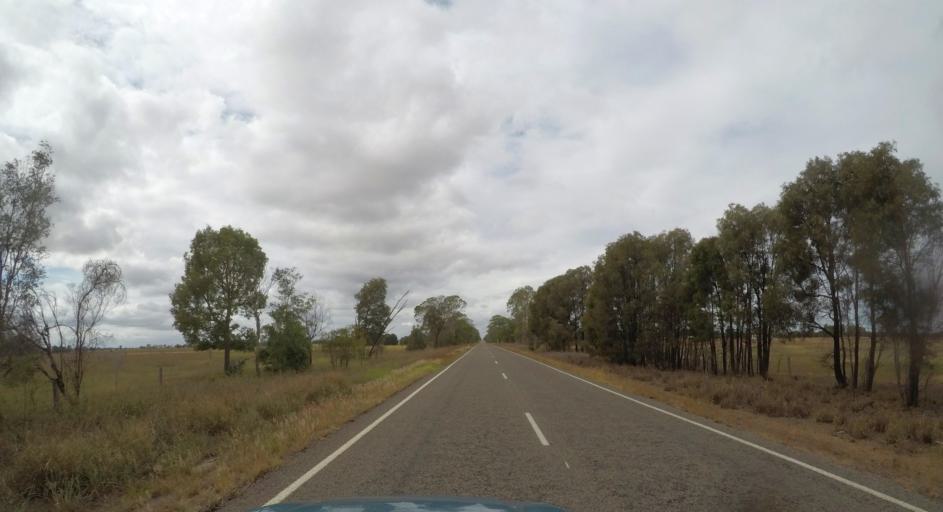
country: AU
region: Queensland
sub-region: South Burnett
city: Kingaroy
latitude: -26.3919
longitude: 151.2173
